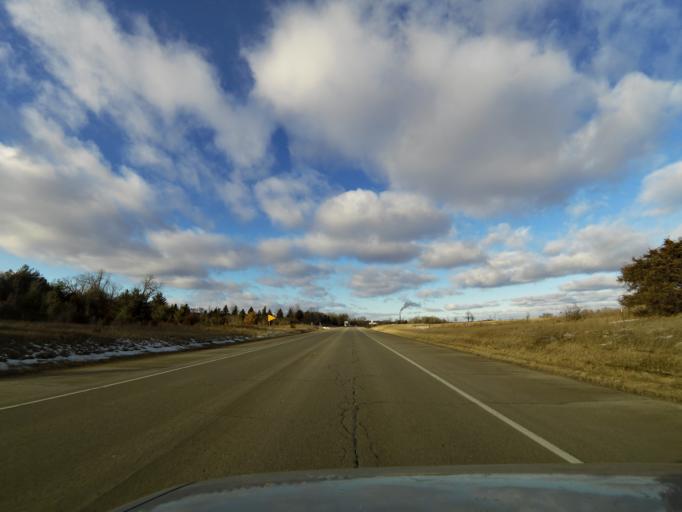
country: US
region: Wisconsin
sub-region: Saint Croix County
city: Hudson
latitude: 44.9836
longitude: -92.7785
